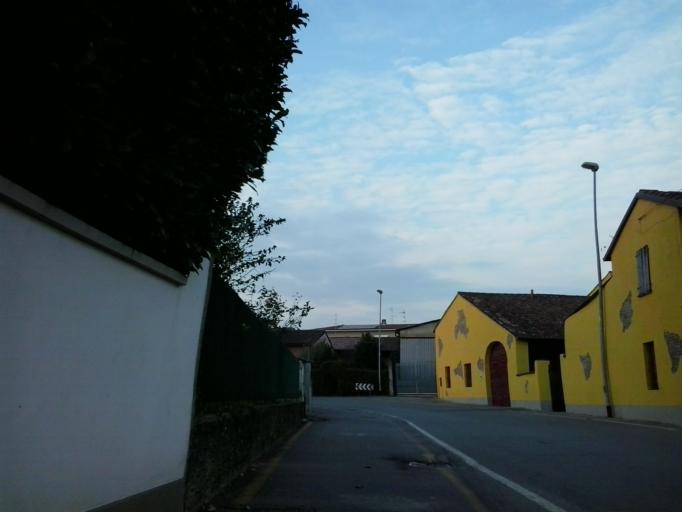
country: IT
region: Lombardy
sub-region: Provincia di Brescia
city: Azzano Mella
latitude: 45.4221
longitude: 10.1219
